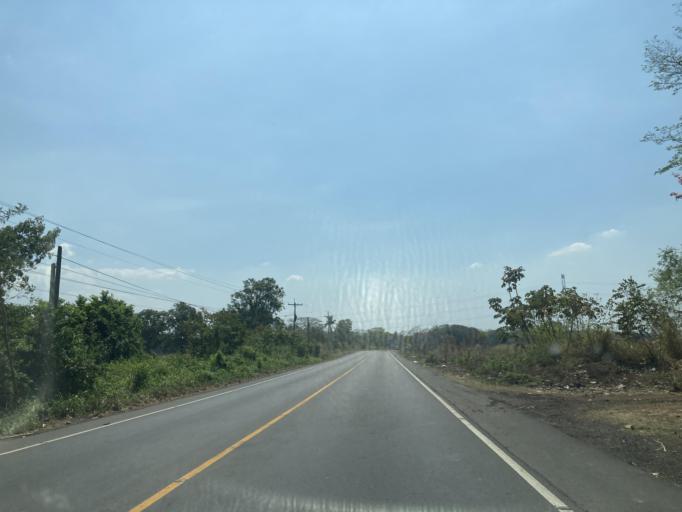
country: GT
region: Escuintla
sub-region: Municipio de Escuintla
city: Escuintla
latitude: 14.2557
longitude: -90.7444
